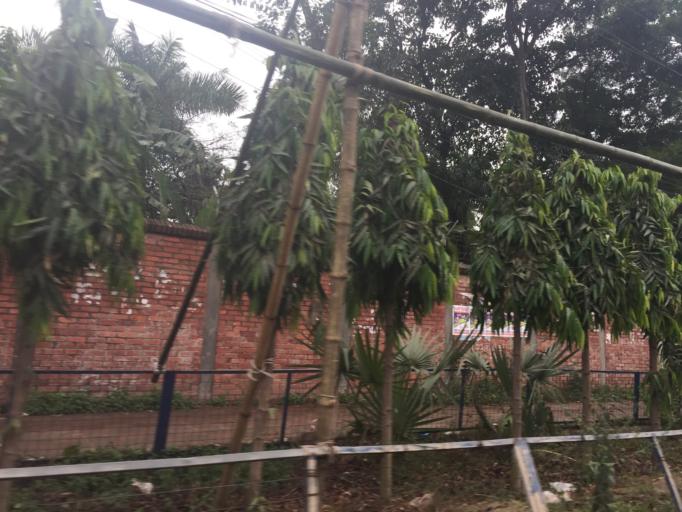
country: BD
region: Dhaka
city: Azimpur
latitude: 23.7754
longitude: 90.3719
